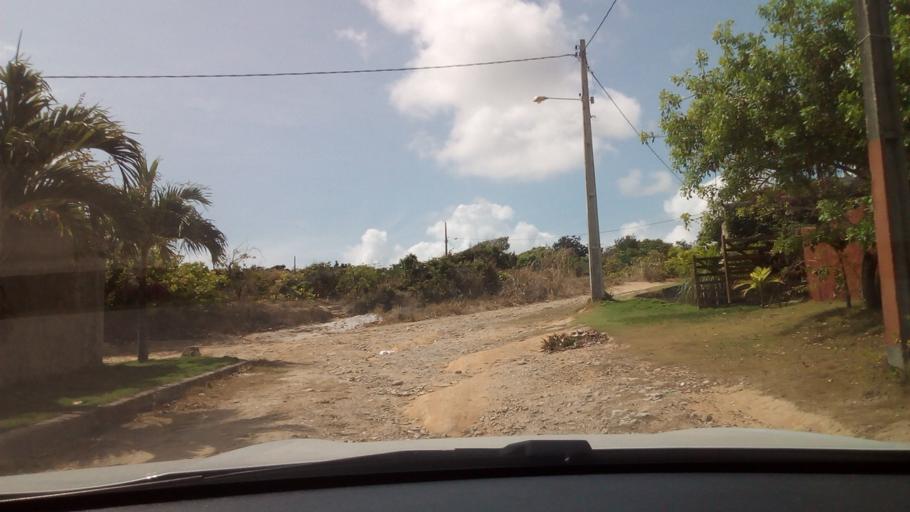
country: BR
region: Paraiba
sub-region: Conde
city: Conde
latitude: -7.3162
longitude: -34.8037
